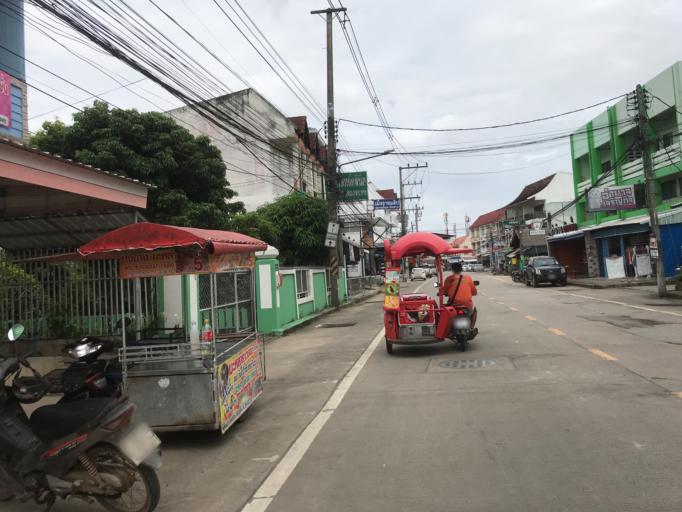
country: TH
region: Chiang Rai
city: Chiang Rai
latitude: 19.9015
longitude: 99.8190
